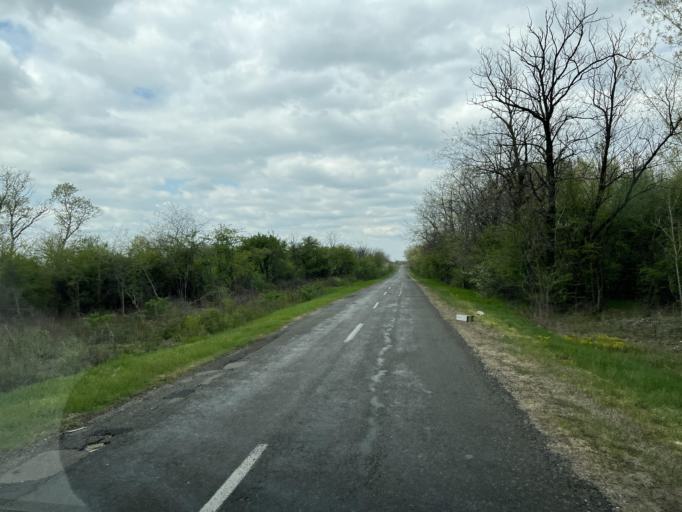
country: HU
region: Pest
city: Orkeny
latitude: 47.1196
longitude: 19.3556
